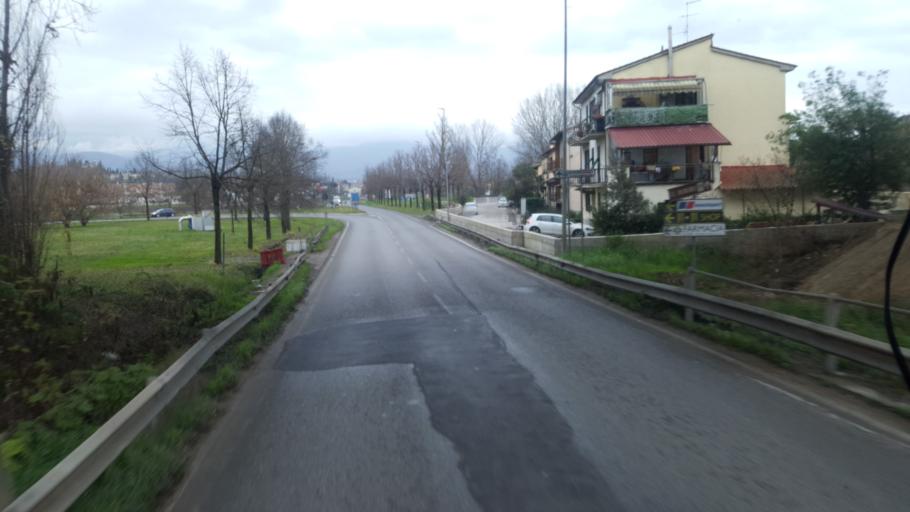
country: IT
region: Tuscany
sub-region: Province of Arezzo
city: Terranuova Bracciolini
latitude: 43.5449
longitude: 11.5726
